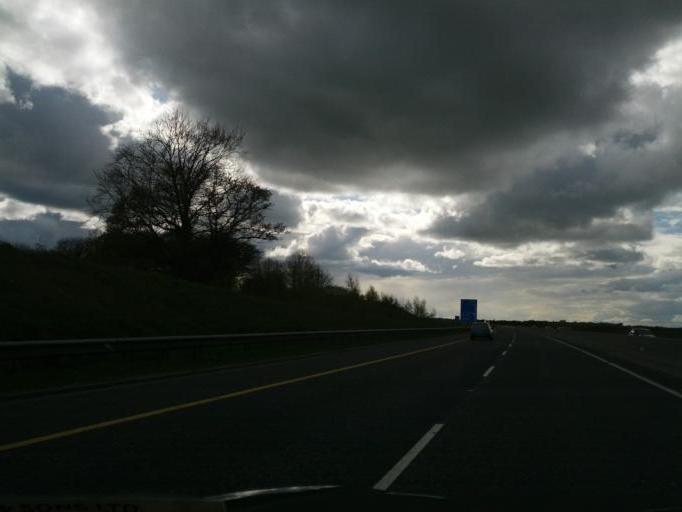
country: IE
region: Leinster
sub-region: An Iarmhi
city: Kilbeggan
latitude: 53.3592
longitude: -7.4674
